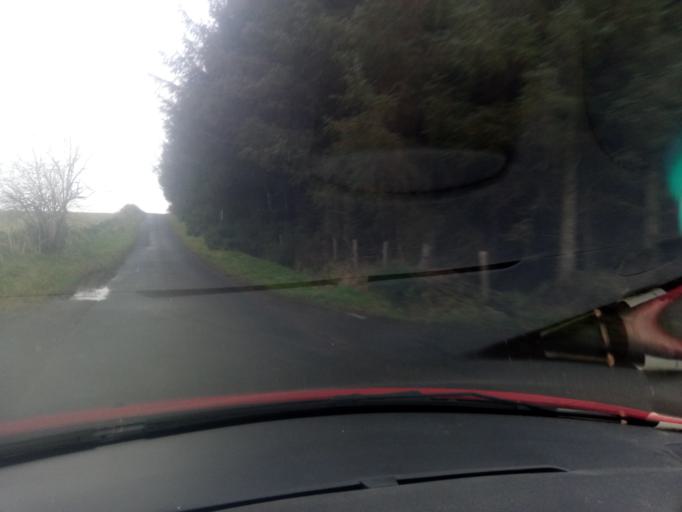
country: GB
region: Scotland
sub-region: The Scottish Borders
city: Jedburgh
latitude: 55.4838
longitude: -2.5848
